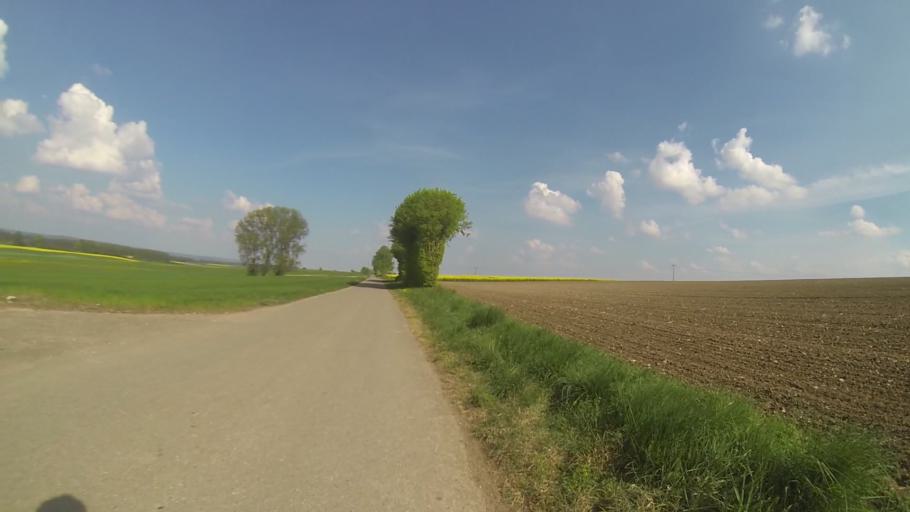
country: DE
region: Baden-Wuerttemberg
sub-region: Tuebingen Region
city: Ballendorf
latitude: 48.6026
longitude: 10.0952
